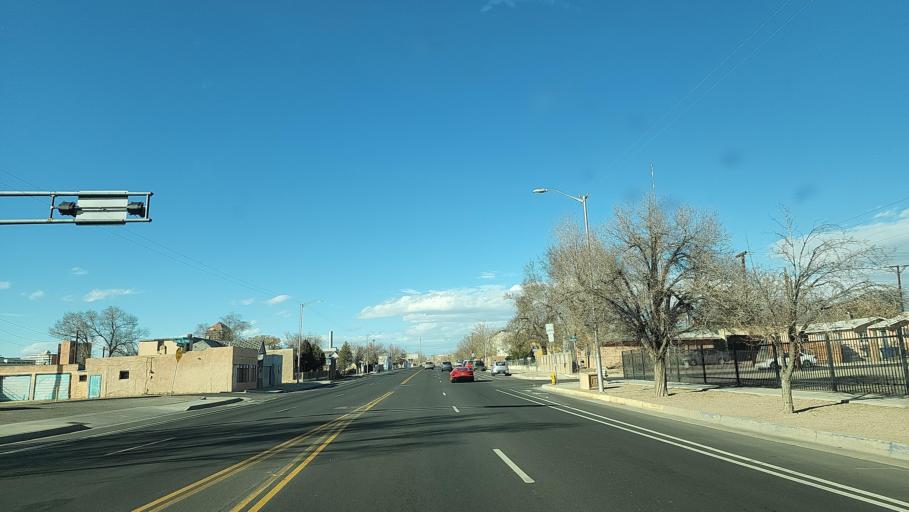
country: US
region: New Mexico
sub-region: Bernalillo County
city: Albuquerque
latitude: 35.0751
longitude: -106.6457
